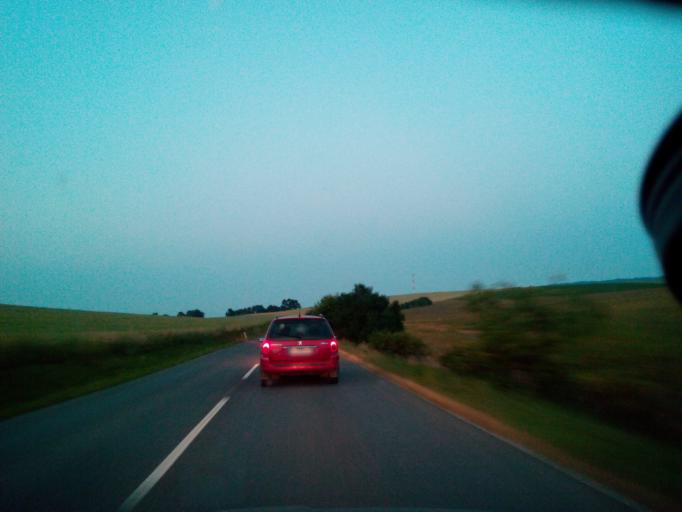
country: SK
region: Presovsky
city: Spisske Podhradie
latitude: 48.9438
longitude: 20.6677
